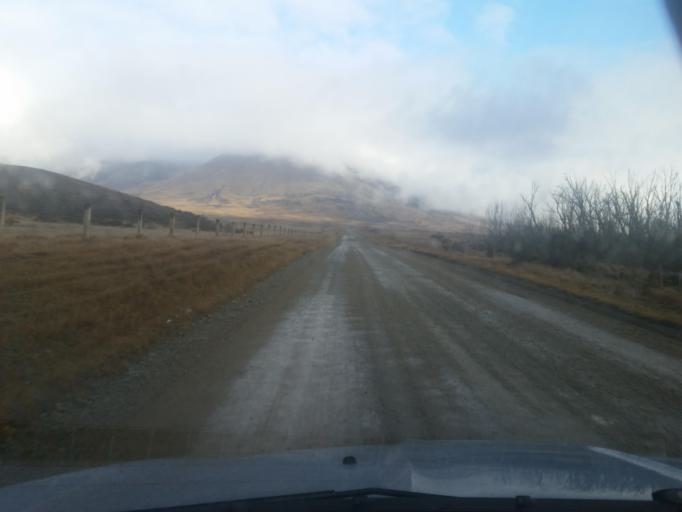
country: NZ
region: Canterbury
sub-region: Ashburton District
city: Methven
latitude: -43.6158
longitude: 171.0911
